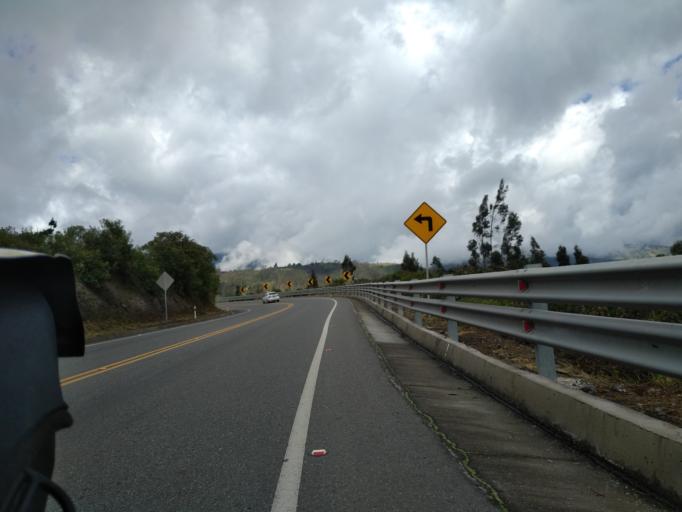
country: EC
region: Tungurahua
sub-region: Canton Quero
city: Quero
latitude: -1.4949
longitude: -78.5247
